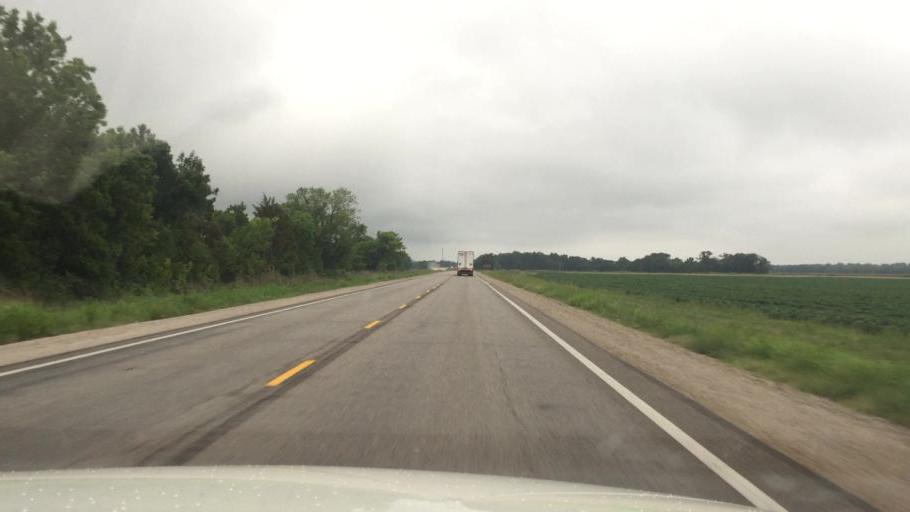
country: US
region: Kansas
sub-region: Montgomery County
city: Coffeyville
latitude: 37.1247
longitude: -95.5810
